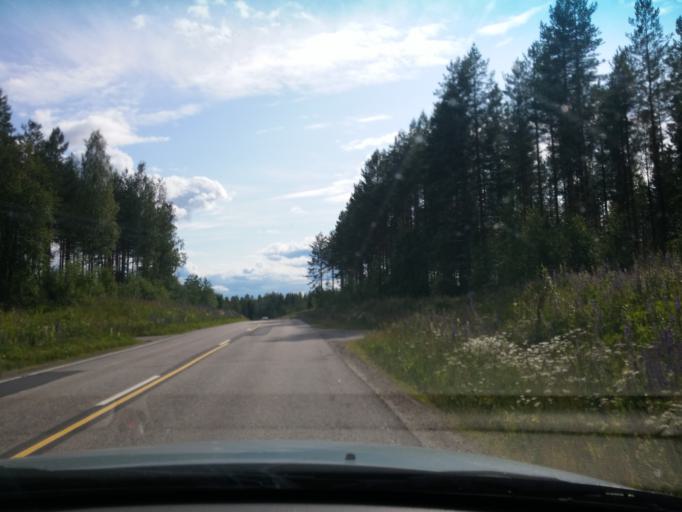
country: FI
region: Central Finland
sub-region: Keuruu
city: Keuruu
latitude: 62.3360
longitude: 24.7347
